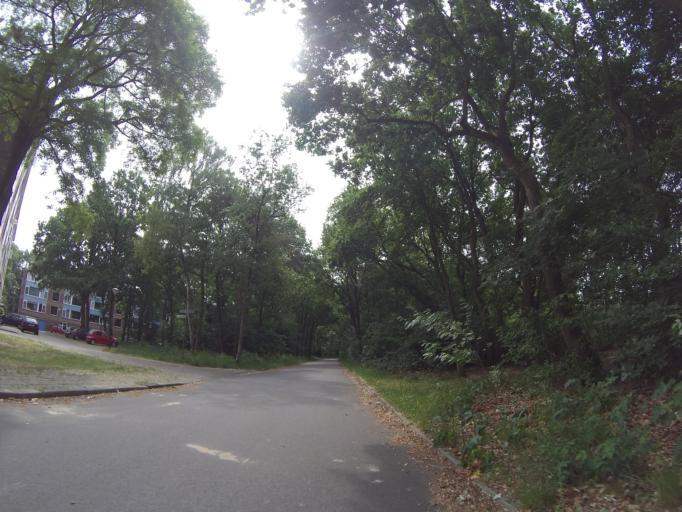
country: NL
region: Utrecht
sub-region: Gemeente Zeist
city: Zeist
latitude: 52.1133
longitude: 5.2816
